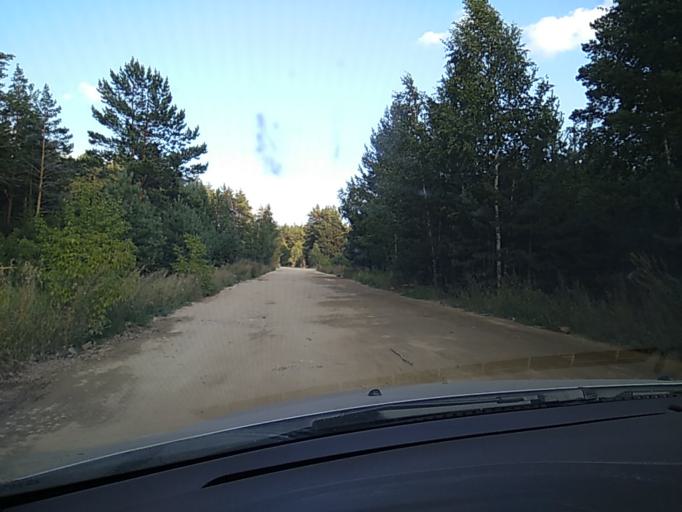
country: RU
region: Chelyabinsk
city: Kyshtym
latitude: 55.6861
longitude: 60.5642
